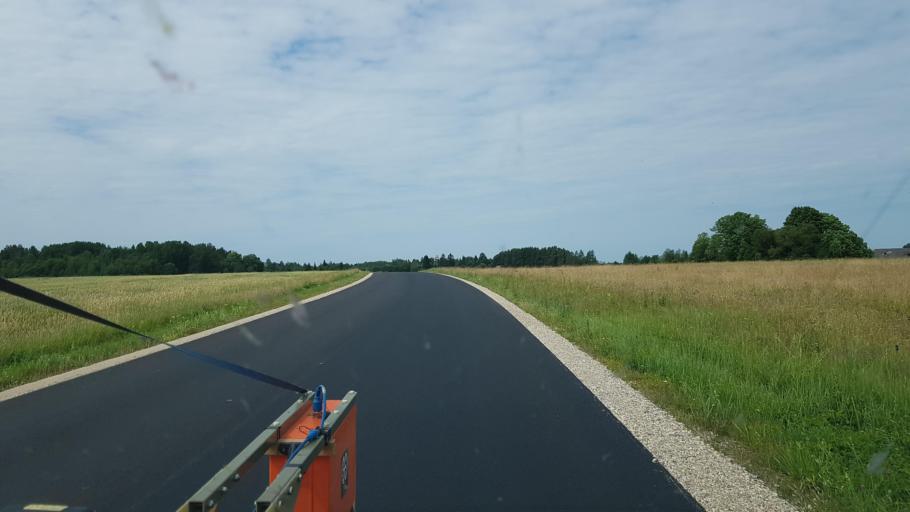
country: EE
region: Paernumaa
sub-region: Halinga vald
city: Parnu-Jaagupi
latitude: 58.6202
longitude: 24.3109
